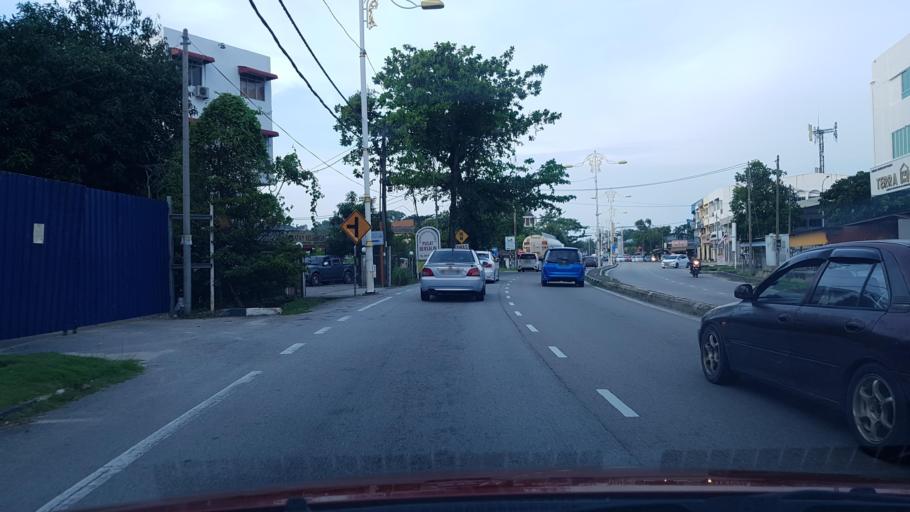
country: MY
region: Terengganu
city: Kuala Terengganu
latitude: 5.3153
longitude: 103.1482
